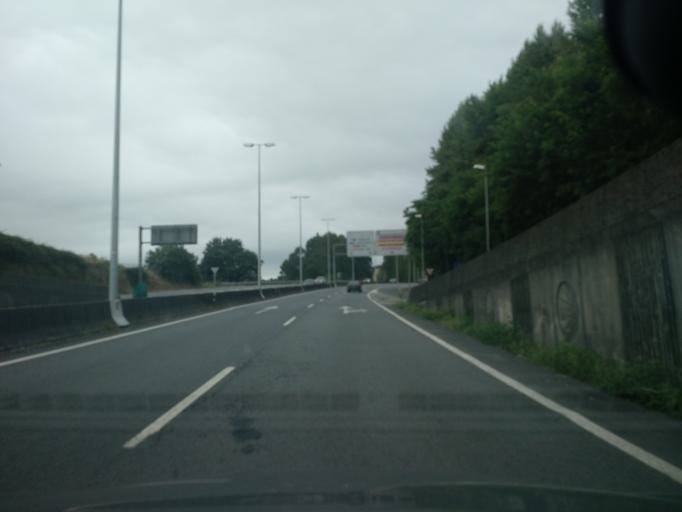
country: ES
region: Galicia
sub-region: Provincia da Coruna
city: Santiago de Compostela
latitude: 42.8859
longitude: -8.5108
